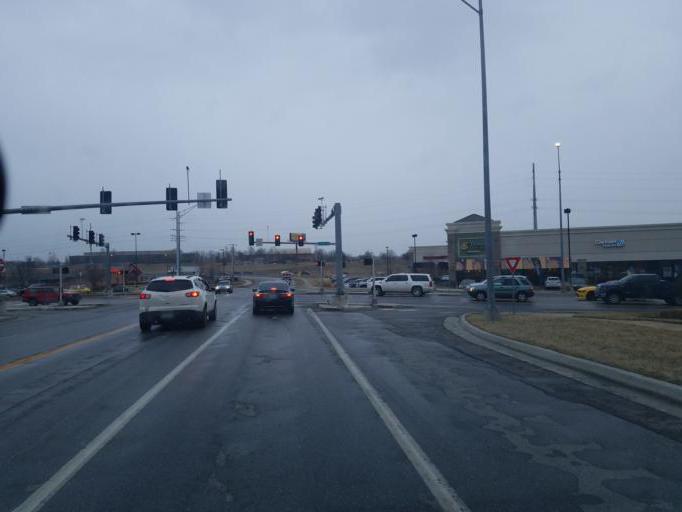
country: US
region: Missouri
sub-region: Boone County
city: Columbia
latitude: 38.9484
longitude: -92.2963
